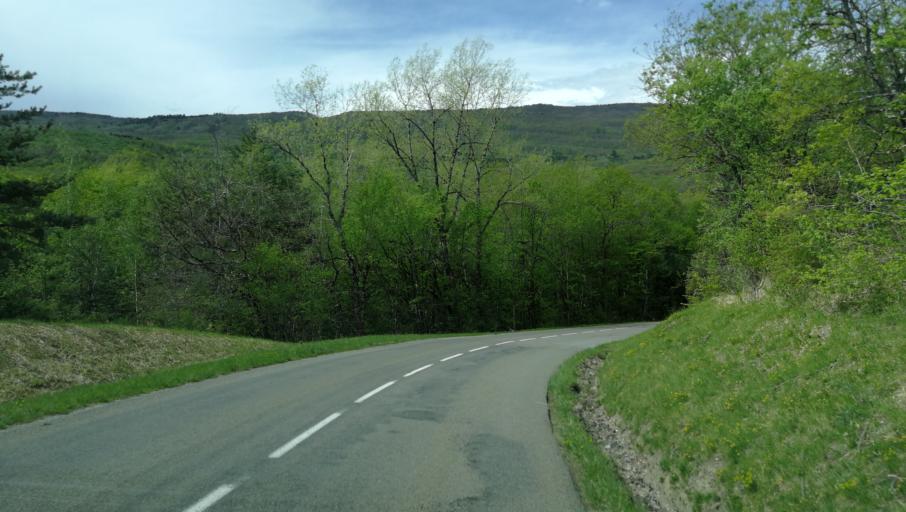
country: FR
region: Rhone-Alpes
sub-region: Departement de l'Ain
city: Bellegarde-sur-Valserine
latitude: 46.0311
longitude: 5.7820
